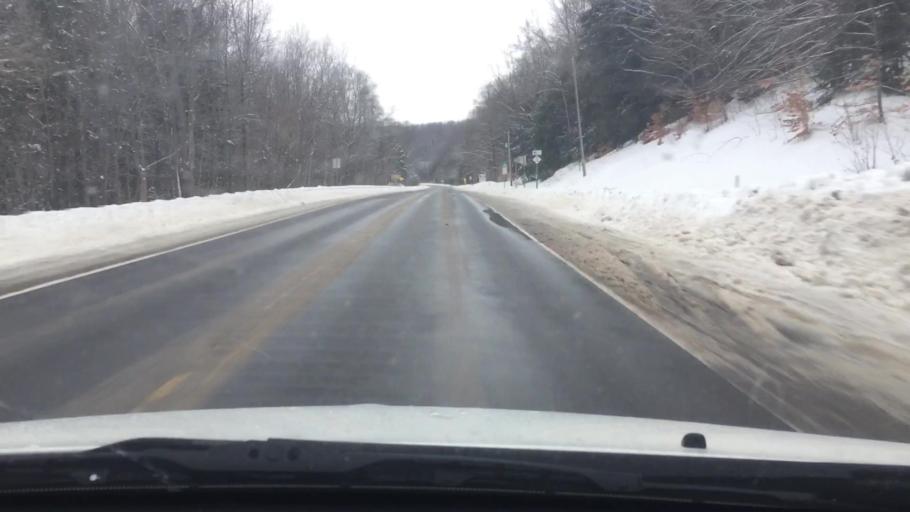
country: US
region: Michigan
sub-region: Charlevoix County
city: East Jordan
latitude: 45.1183
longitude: -85.0617
